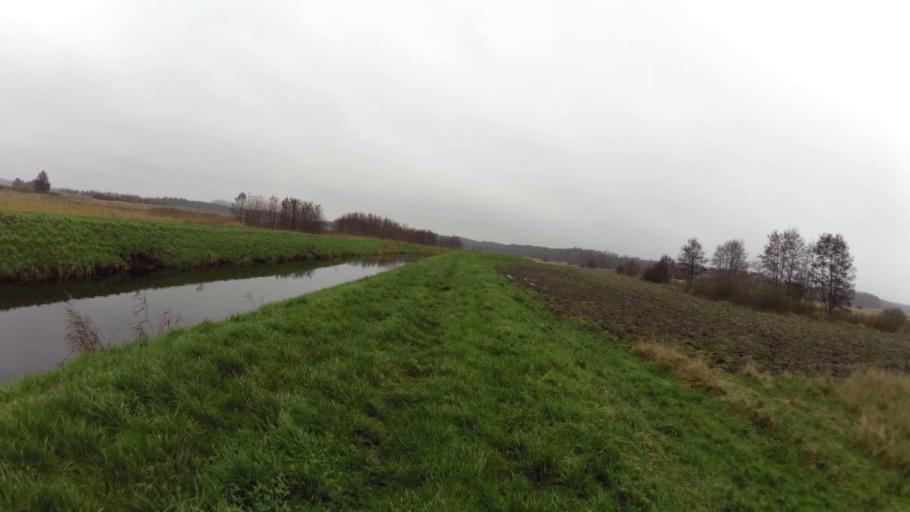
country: PL
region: West Pomeranian Voivodeship
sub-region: Koszalin
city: Koszalin
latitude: 54.2413
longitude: 16.1289
